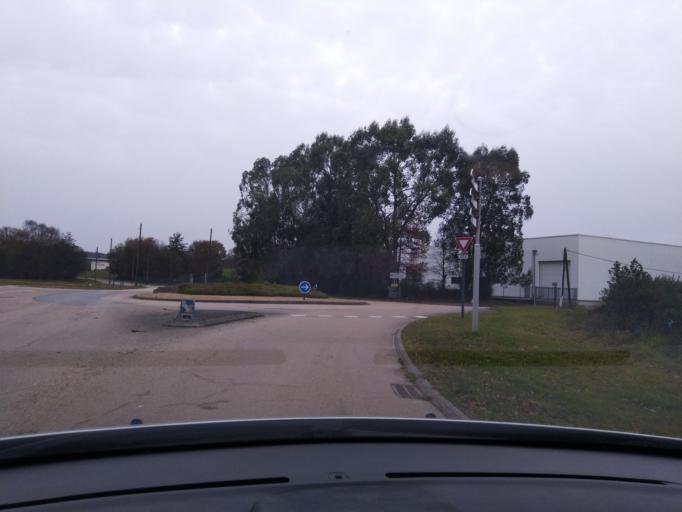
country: FR
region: Brittany
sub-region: Departement du Finistere
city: Guerlesquin
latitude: 48.5127
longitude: -3.5844
